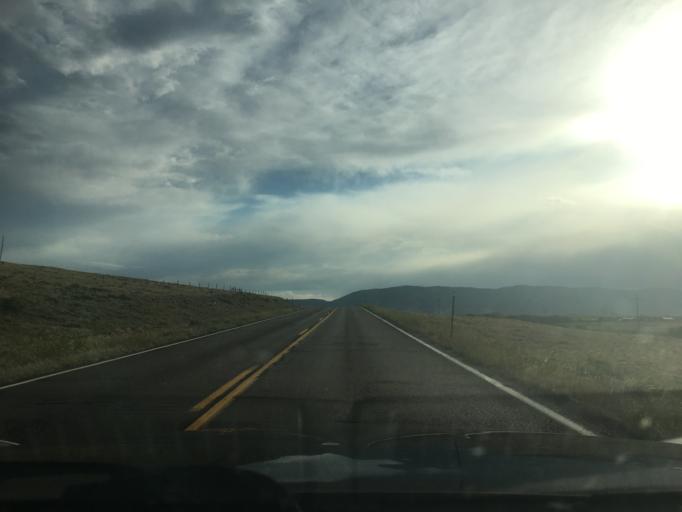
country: US
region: Wyoming
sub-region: Albany County
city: Laramie
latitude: 41.2847
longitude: -106.0529
